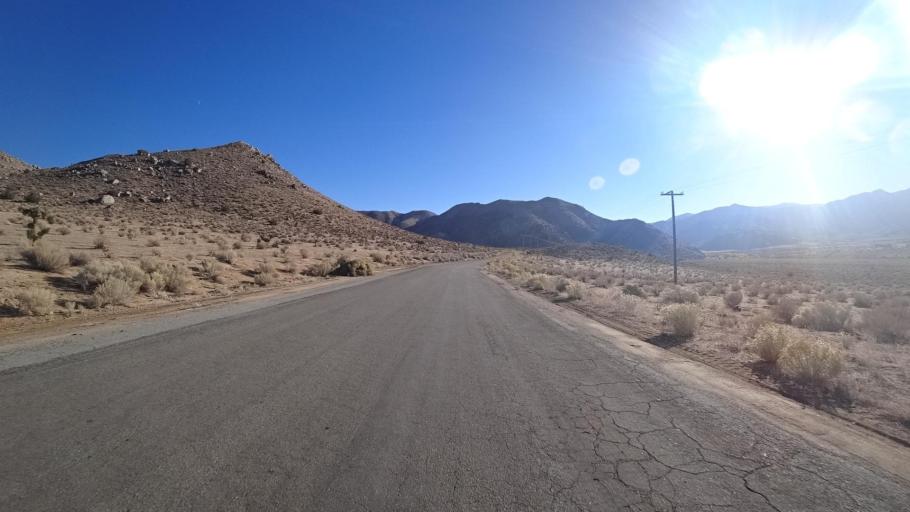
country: US
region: California
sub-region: Kern County
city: Weldon
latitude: 35.5930
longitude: -118.2400
